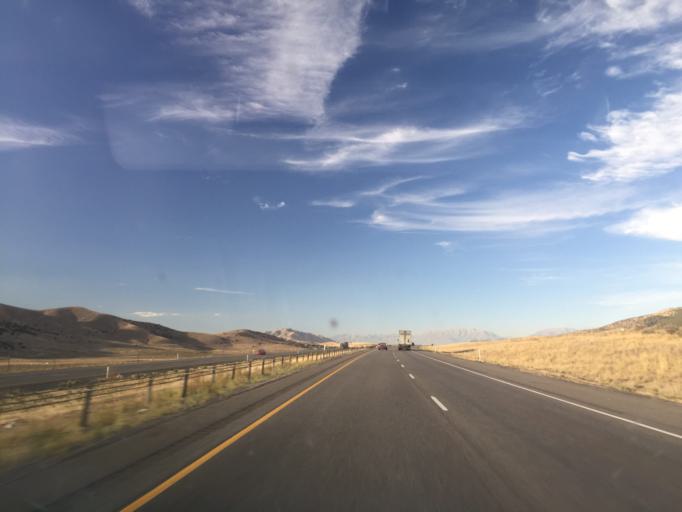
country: US
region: Utah
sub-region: Juab County
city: Mona
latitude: 39.8956
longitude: -111.8279
